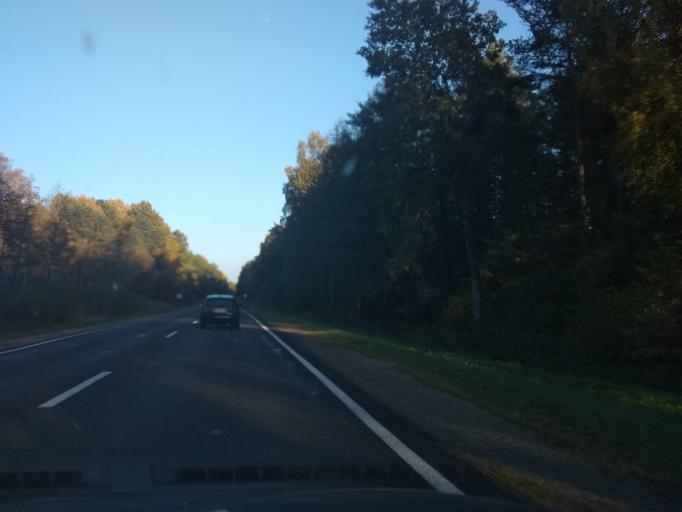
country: BY
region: Grodnenskaya
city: Zel'va
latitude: 53.1415
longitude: 24.6521
